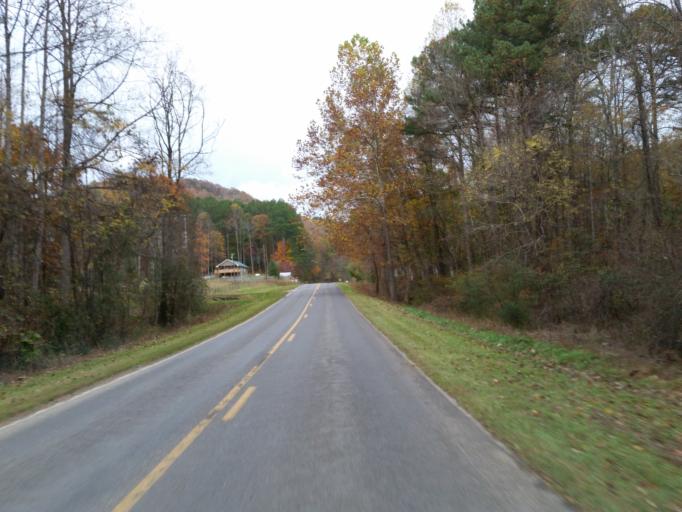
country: US
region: Georgia
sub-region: Fannin County
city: Blue Ridge
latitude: 34.6834
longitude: -84.2690
